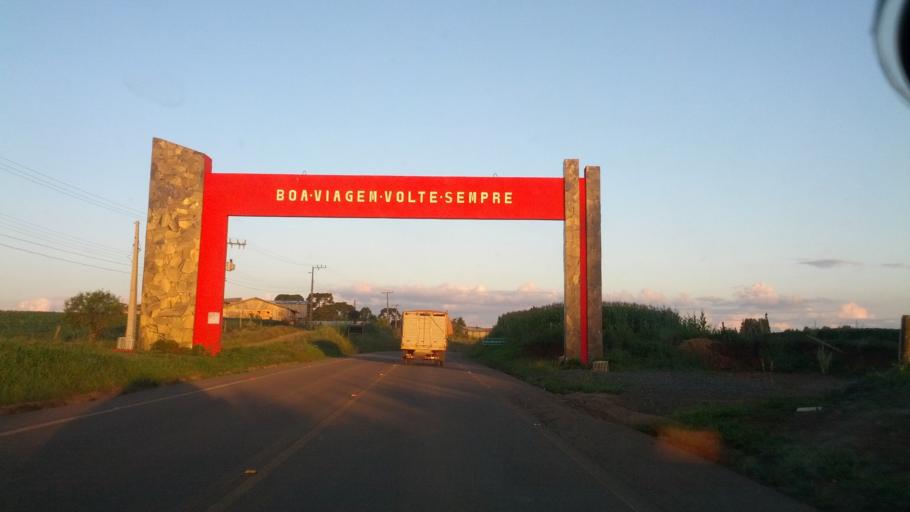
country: BR
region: Rio Grande do Sul
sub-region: Vacaria
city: Estrela
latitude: -27.7970
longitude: -50.8658
